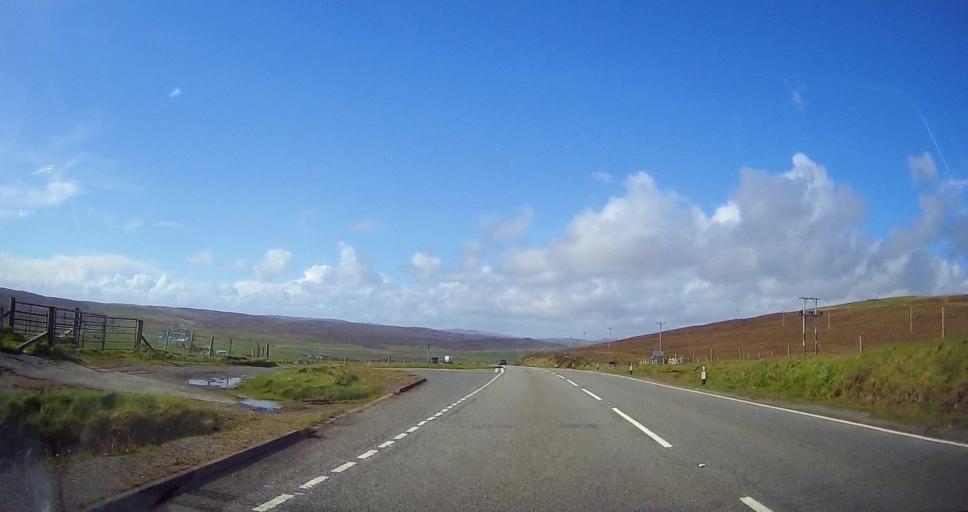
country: GB
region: Scotland
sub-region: Shetland Islands
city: Lerwick
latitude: 60.1759
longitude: -1.2229
